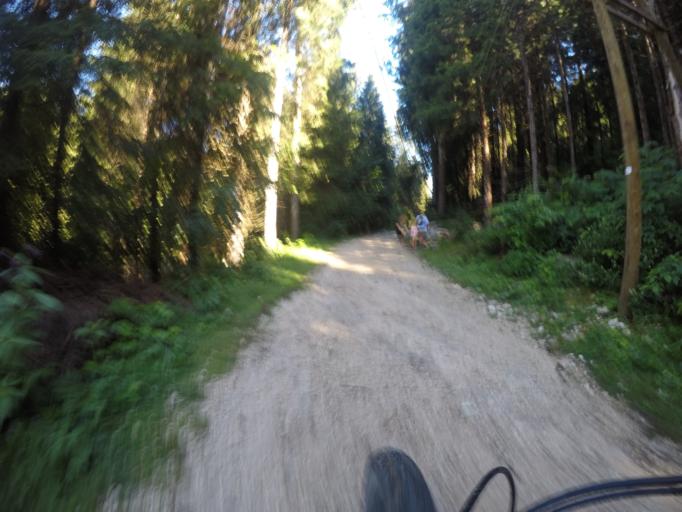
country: IT
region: Veneto
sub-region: Provincia di Vicenza
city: Cogollo del Cengio
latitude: 45.8289
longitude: 11.4368
